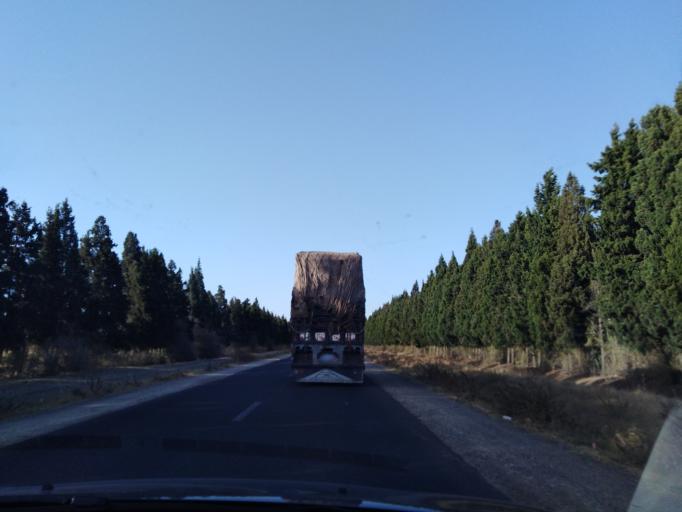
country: MA
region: Doukkala-Abda
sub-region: Safi
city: Safi
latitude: 32.5035
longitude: -8.9229
